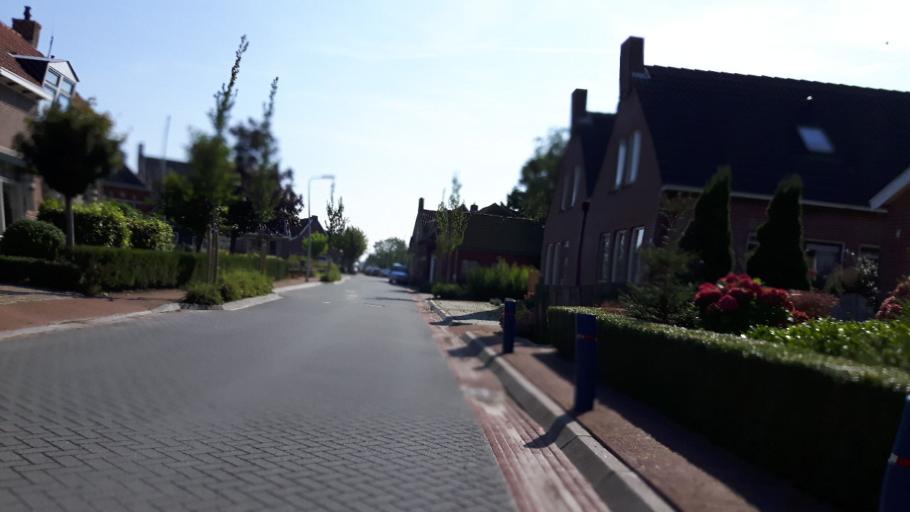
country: NL
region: Friesland
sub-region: Gemeente Ferwerderadiel
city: Ferwert
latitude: 53.3525
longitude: 5.8606
